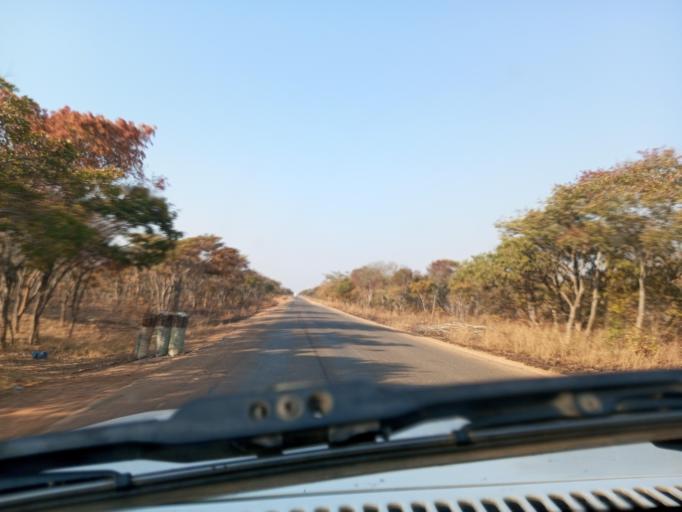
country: ZM
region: Northern
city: Mpika
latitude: -12.4005
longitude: 31.0888
